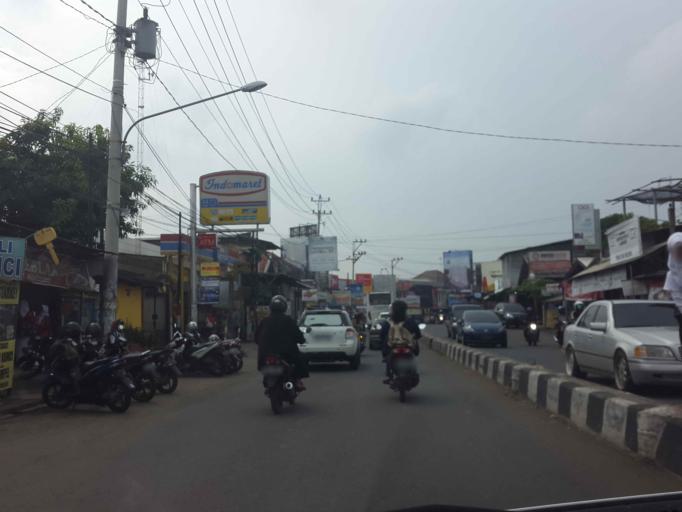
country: ID
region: Central Java
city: Semarang
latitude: -7.0540
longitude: 110.4319
